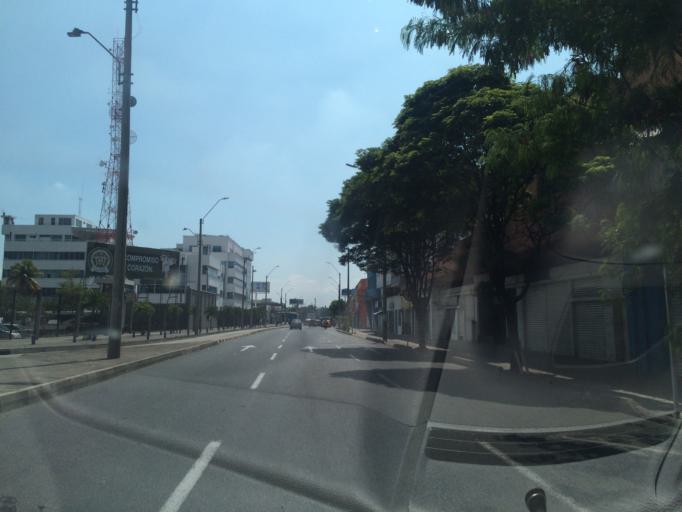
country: CO
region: Valle del Cauca
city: Cali
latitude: 3.4574
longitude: -76.5276
